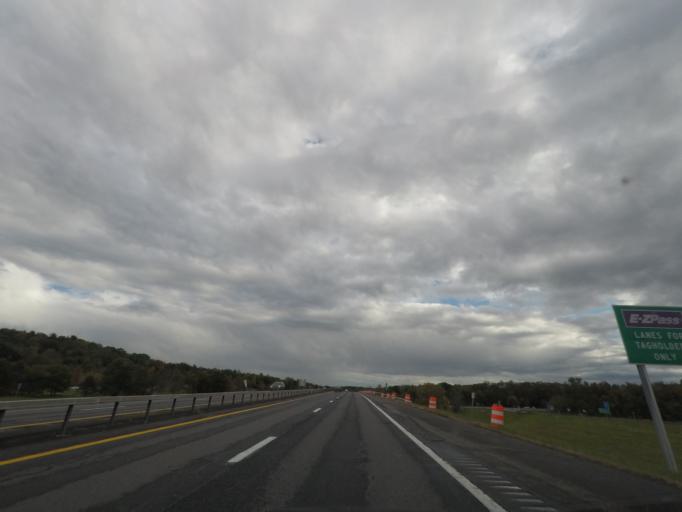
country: US
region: New York
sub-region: Columbia County
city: Niverville
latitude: 42.4908
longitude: -73.6806
